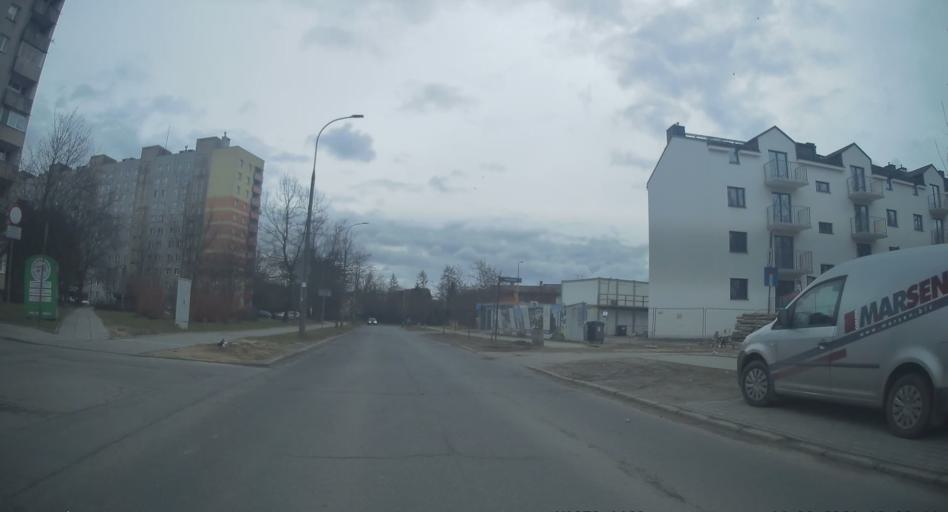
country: PL
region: Lesser Poland Voivodeship
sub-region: Powiat wielicki
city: Czarnochowice
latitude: 50.0107
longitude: 20.0176
